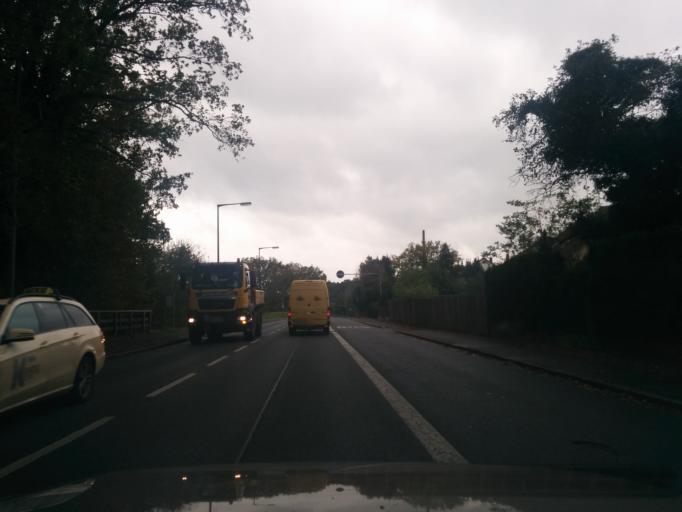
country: DE
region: Bavaria
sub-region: Regierungsbezirk Mittelfranken
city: Uttenreuth
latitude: 49.5967
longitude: 11.0619
